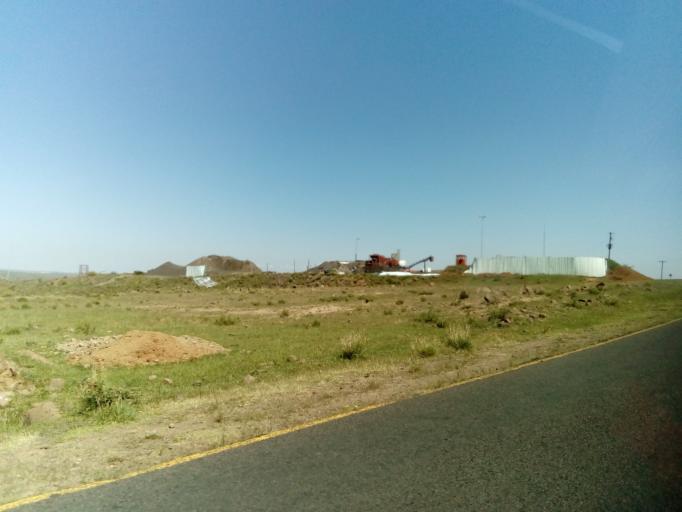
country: LS
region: Berea
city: Teyateyaneng
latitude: -29.2148
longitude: 27.8471
